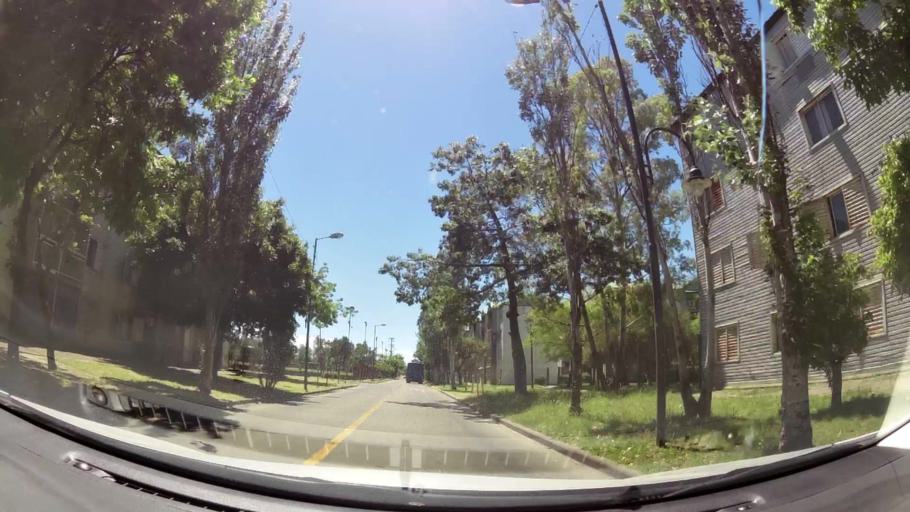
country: AR
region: Buenos Aires
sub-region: Partido de Tigre
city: Tigre
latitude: -34.4597
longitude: -58.5578
